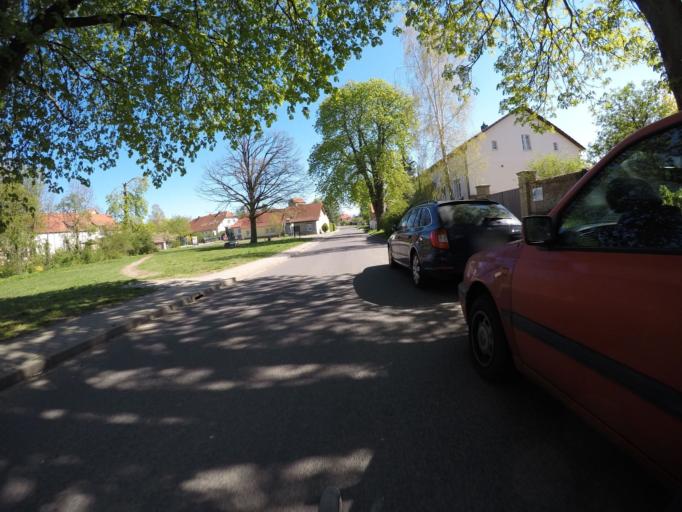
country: DE
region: Brandenburg
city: Werftpfuhl
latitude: 52.6383
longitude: 13.7960
